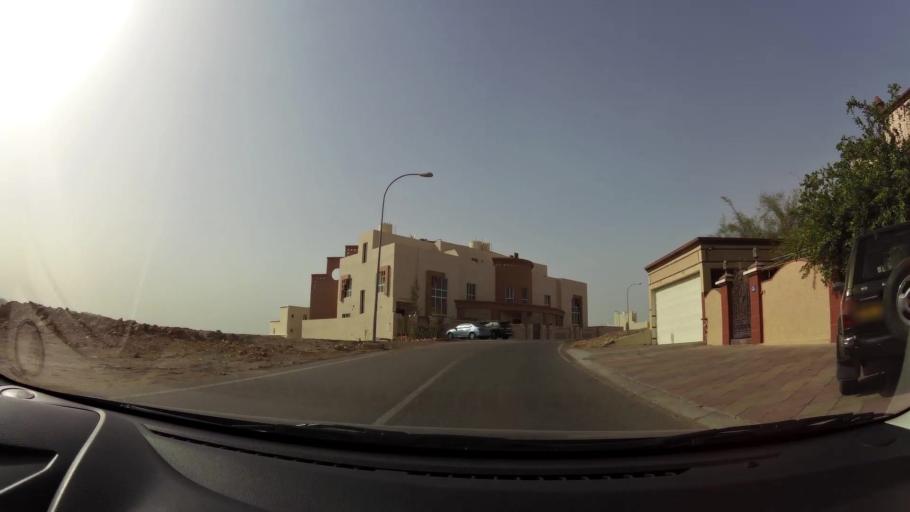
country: OM
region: Muhafazat Masqat
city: Bawshar
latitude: 23.5566
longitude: 58.3533
